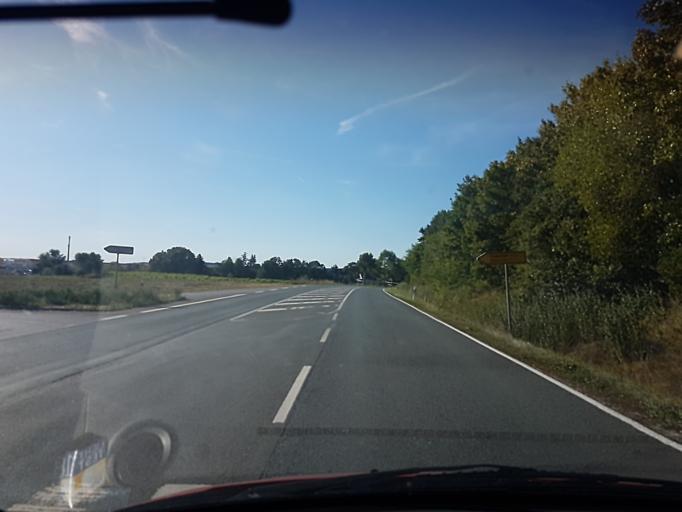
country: DE
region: Bavaria
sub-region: Regierungsbezirk Mittelfranken
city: Adelsdorf
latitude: 49.7074
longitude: 10.9077
